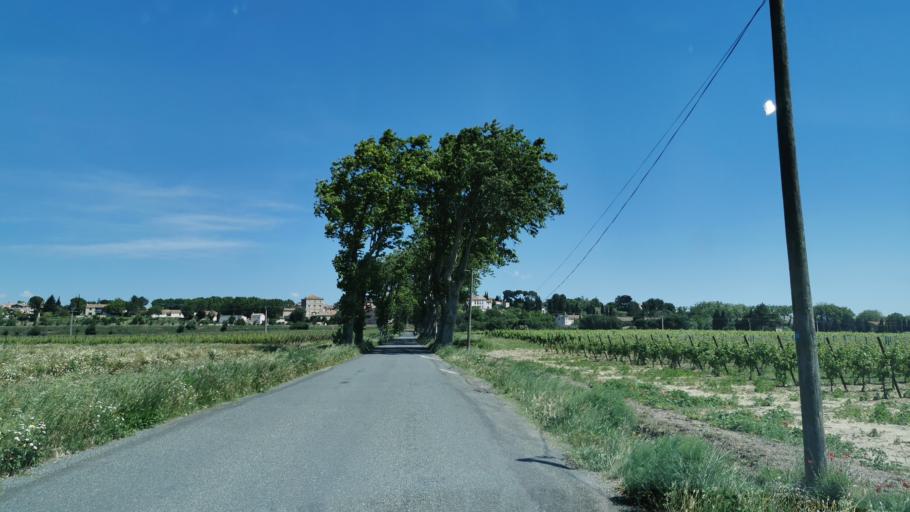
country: FR
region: Languedoc-Roussillon
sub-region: Departement de l'Aude
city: Canet
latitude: 43.2434
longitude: 2.8557
